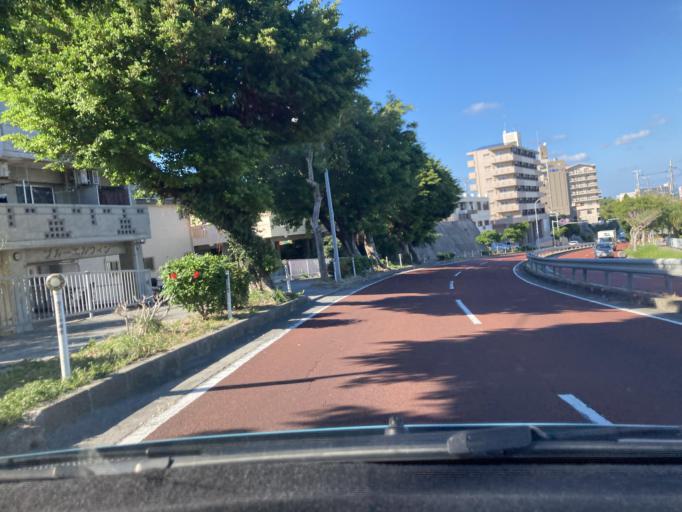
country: JP
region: Okinawa
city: Ginowan
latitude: 26.2610
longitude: 127.7262
